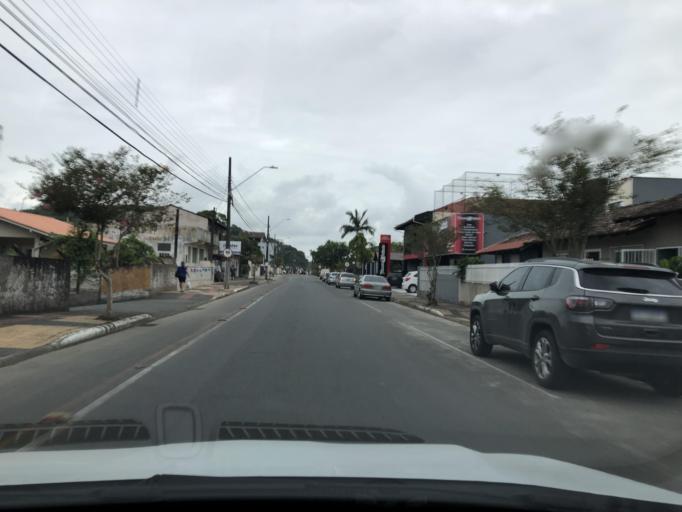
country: BR
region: Santa Catarina
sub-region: Sao Francisco Do Sul
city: Sao Francisco do Sul
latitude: -26.2474
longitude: -48.6270
